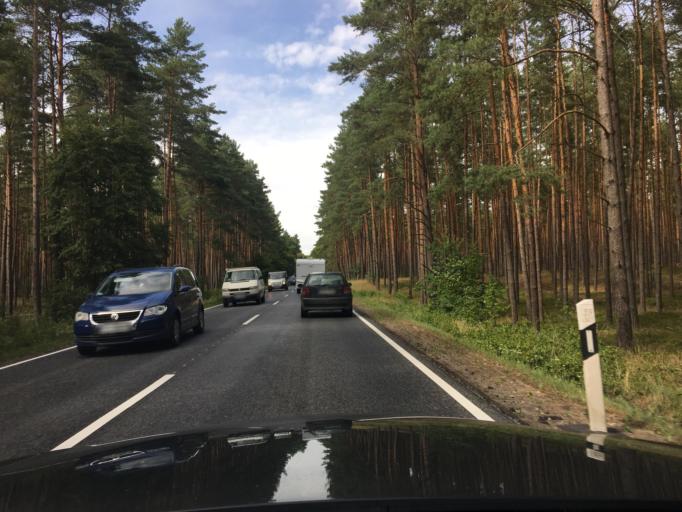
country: DE
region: Brandenburg
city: Furstenberg
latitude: 53.2236
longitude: 13.1217
